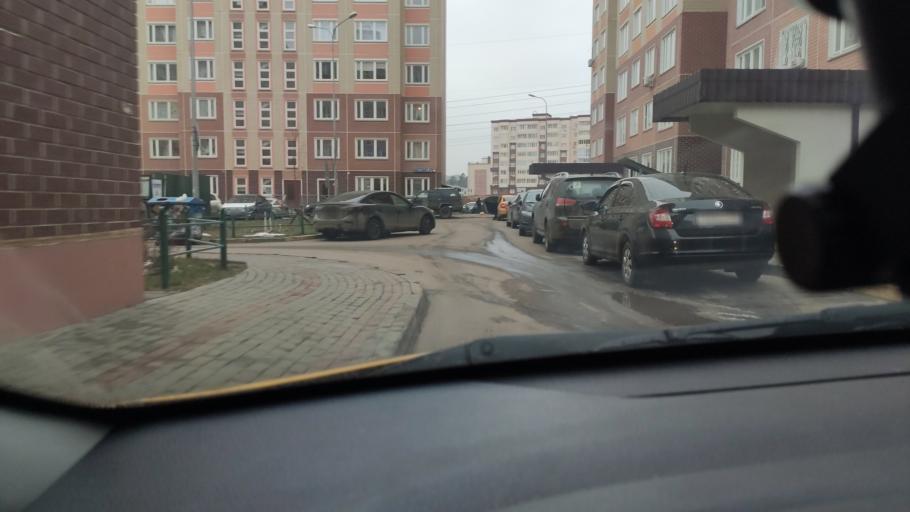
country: RU
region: Moscow
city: Zagor'ye
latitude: 55.5344
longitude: 37.6403
